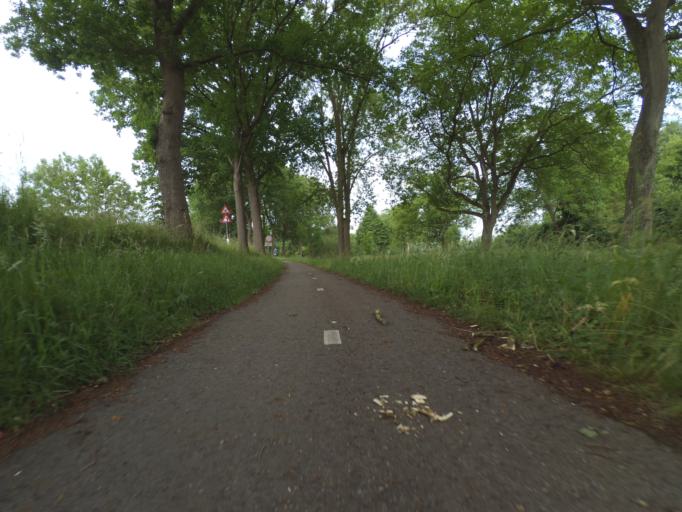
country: NL
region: Gelderland
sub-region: Gemeente Geldermalsen
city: Geldermalsen
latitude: 51.9105
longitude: 5.3271
